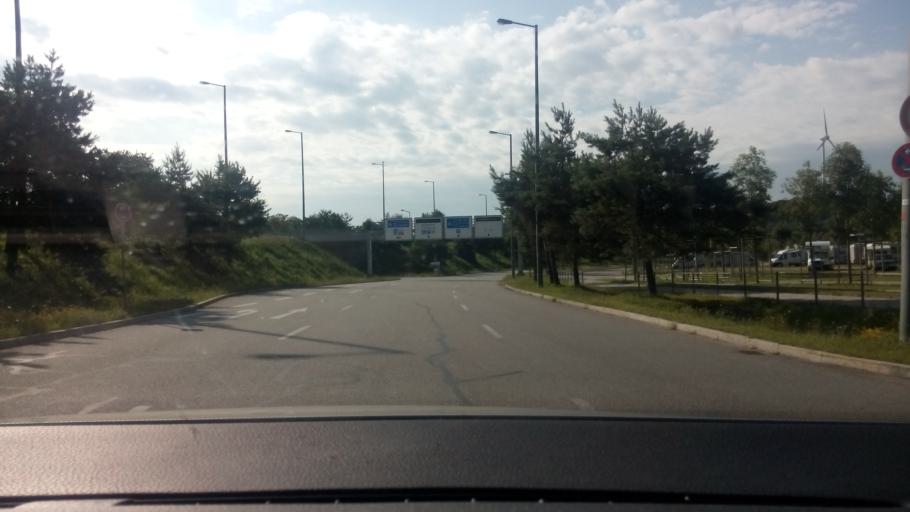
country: DE
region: Bavaria
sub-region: Upper Bavaria
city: Unterfoehring
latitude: 48.2219
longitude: 11.6245
